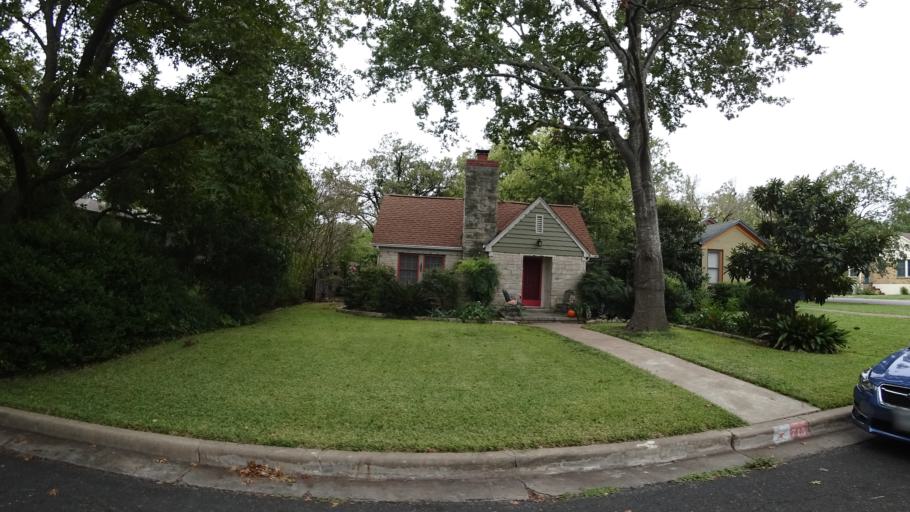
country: US
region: Texas
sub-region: Travis County
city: Austin
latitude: 30.2956
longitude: -97.7281
